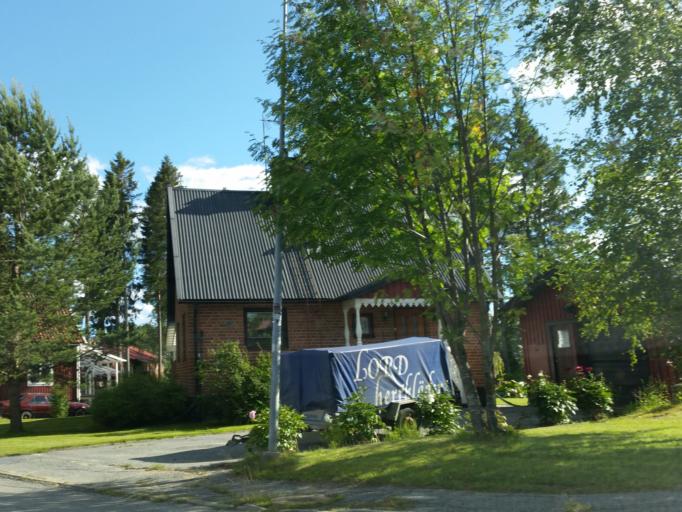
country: SE
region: Vaesterbotten
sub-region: Robertsfors Kommun
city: Robertsfors
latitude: 64.1968
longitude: 20.8486
